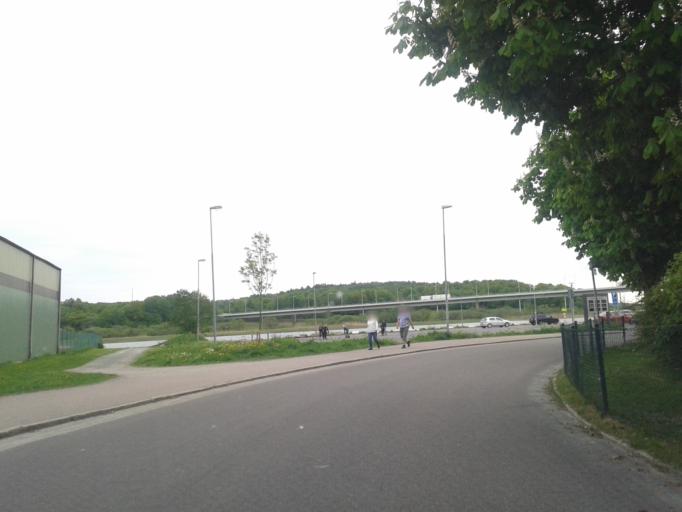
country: SE
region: Vaestra Goetaland
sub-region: Kungalvs Kommun
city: Kungalv
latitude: 57.8675
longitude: 11.9795
